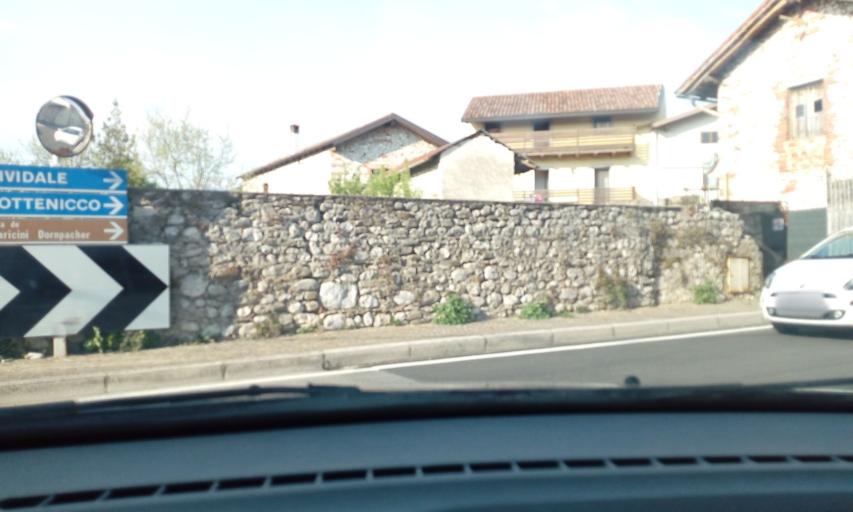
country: IT
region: Friuli Venezia Giulia
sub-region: Provincia di Udine
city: Moimacco
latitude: 46.0915
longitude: 13.3818
